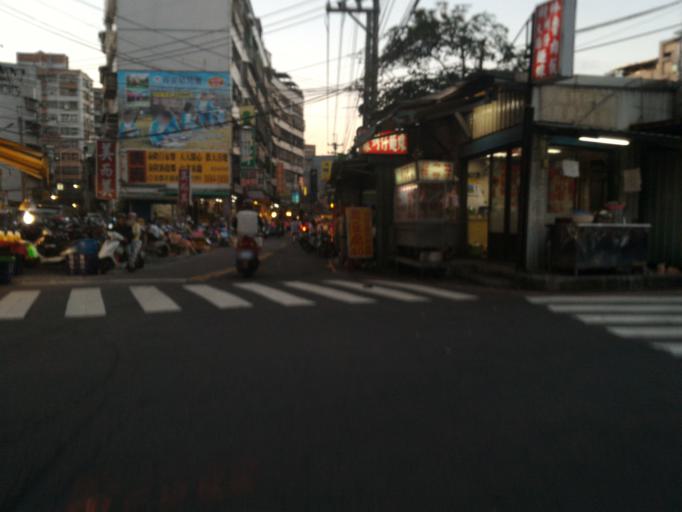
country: TW
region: Taipei
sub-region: Taipei
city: Banqiao
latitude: 24.9780
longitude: 121.4186
